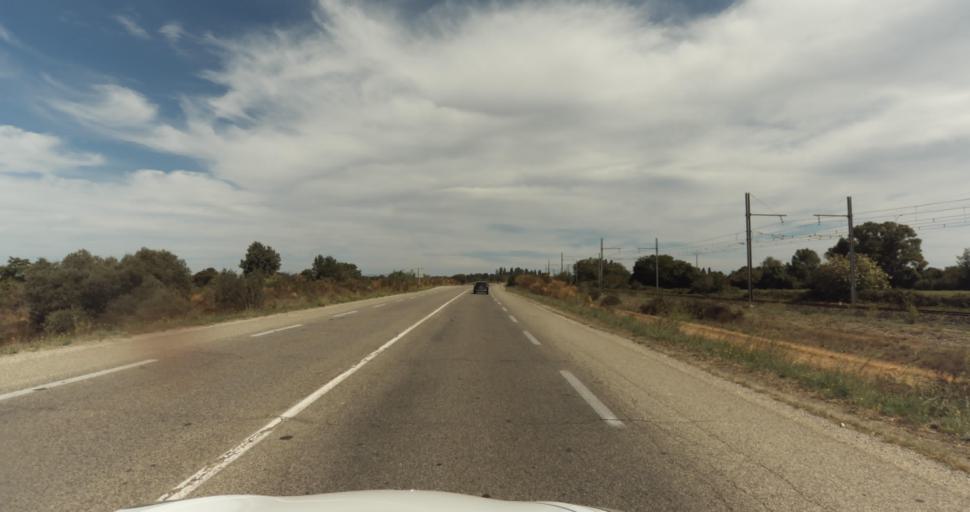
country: FR
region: Provence-Alpes-Cote d'Azur
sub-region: Departement des Bouches-du-Rhone
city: Istres
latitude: 43.5475
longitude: 4.9560
